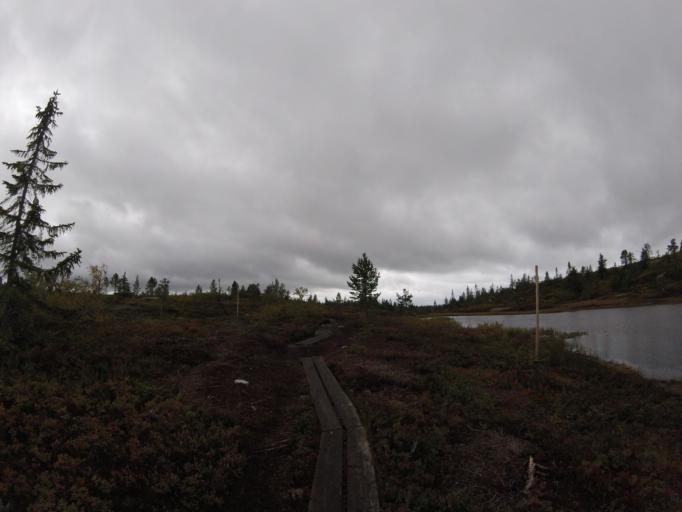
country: NO
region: Buskerud
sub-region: Flesberg
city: Lampeland
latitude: 59.7741
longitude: 9.4054
